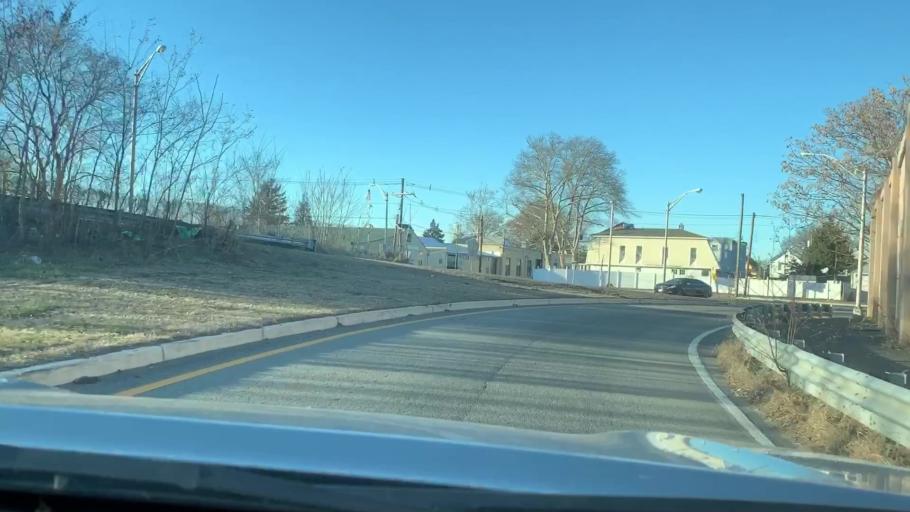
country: US
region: New Jersey
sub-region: Bergen County
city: Little Ferry
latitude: 40.8676
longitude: -74.0423
